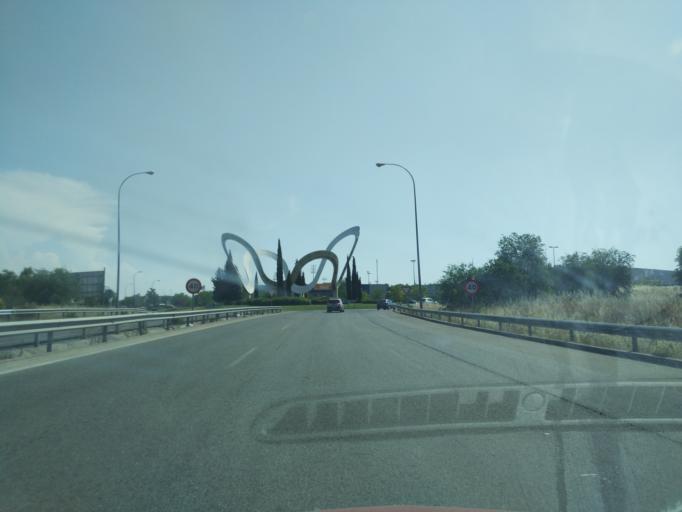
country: ES
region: Madrid
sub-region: Provincia de Madrid
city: Leganes
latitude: 40.3480
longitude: -3.7547
